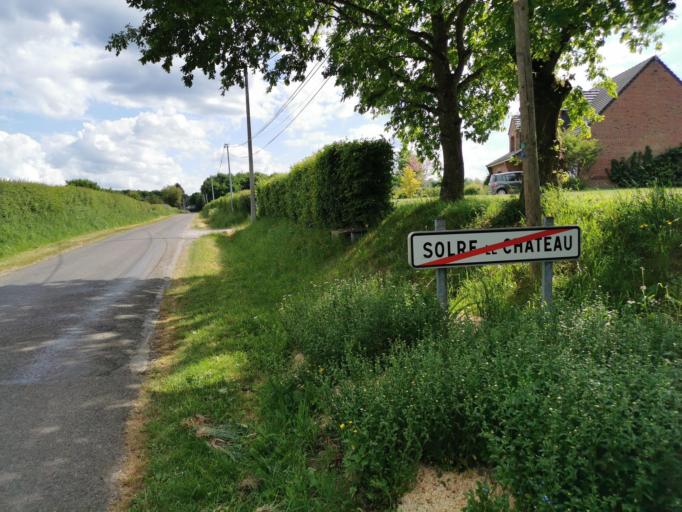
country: FR
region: Nord-Pas-de-Calais
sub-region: Departement du Nord
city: Trelon
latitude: 50.1674
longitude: 4.0990
